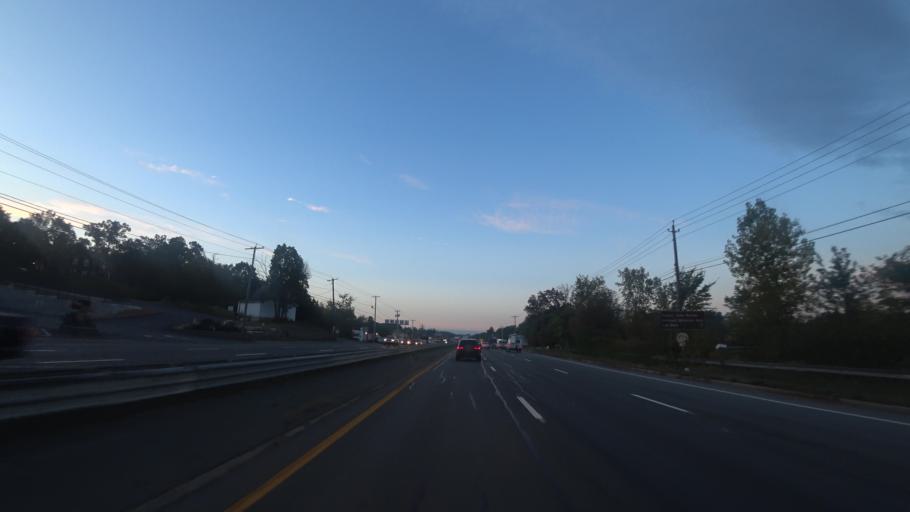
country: US
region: Massachusetts
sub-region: Essex County
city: Saugus
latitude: 42.5000
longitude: -71.0151
